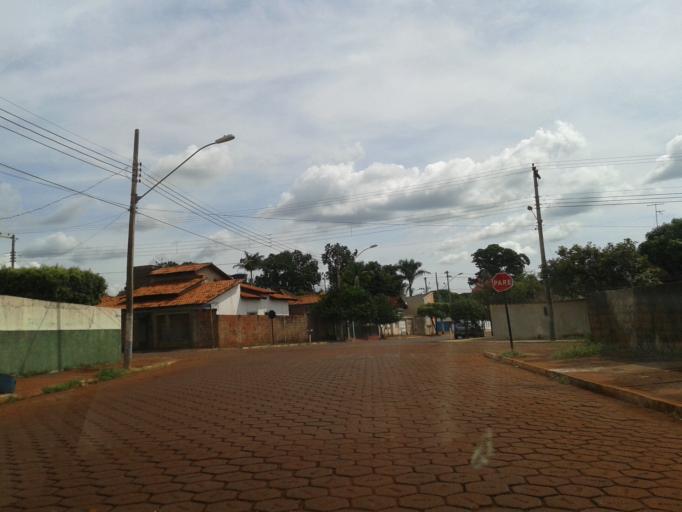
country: BR
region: Minas Gerais
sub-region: Centralina
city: Centralina
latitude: -18.5887
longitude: -49.1997
